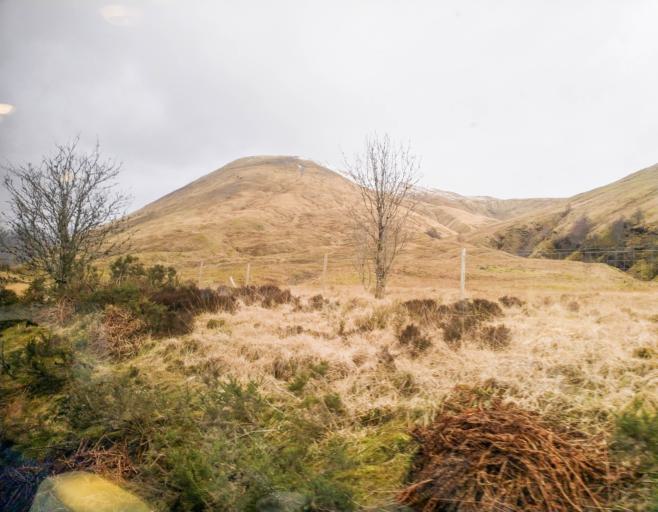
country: GB
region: Scotland
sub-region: Argyll and Bute
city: Garelochhead
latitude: 56.4491
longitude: -4.7083
